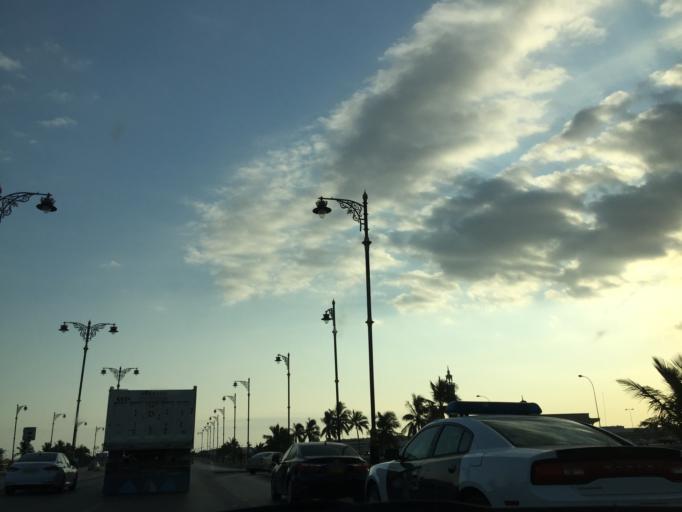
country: OM
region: Zufar
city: Salalah
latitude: 17.0245
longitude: 54.0579
